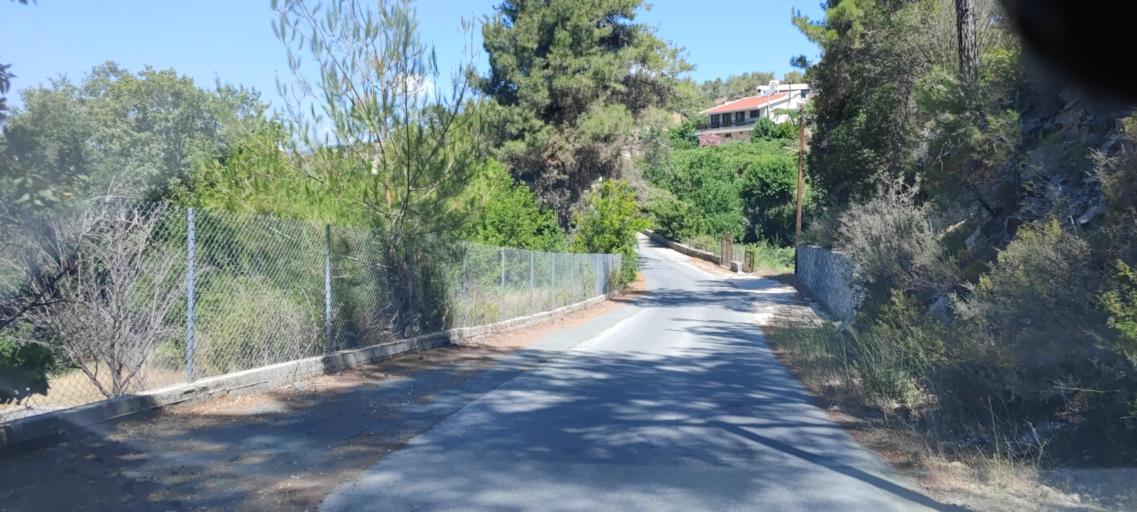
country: CY
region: Lefkosia
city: Kakopetria
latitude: 34.9238
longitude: 32.8110
